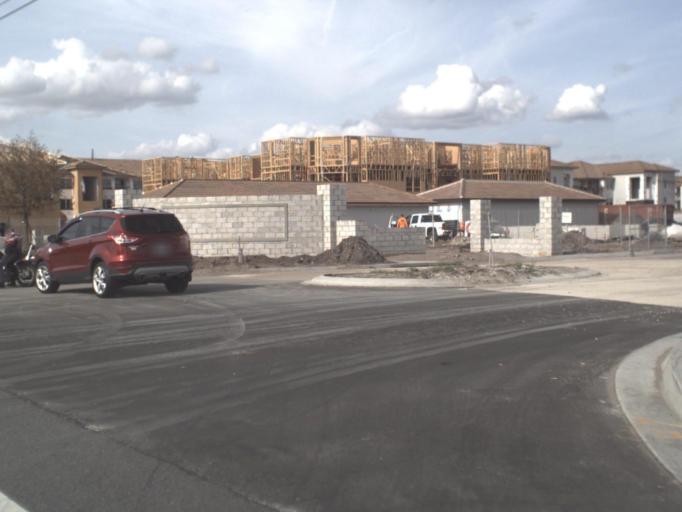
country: US
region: Florida
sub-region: Osceola County
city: Saint Cloud
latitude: 28.3556
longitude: -81.2395
